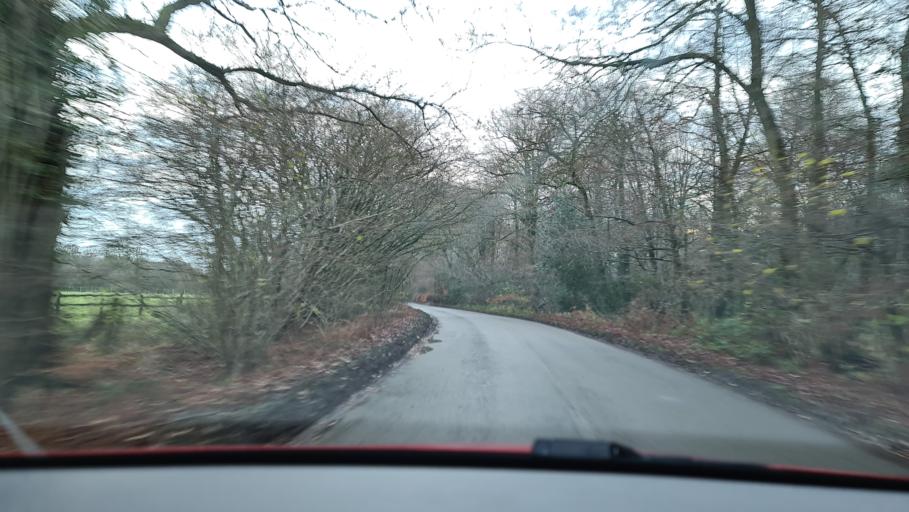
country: GB
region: England
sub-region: Buckinghamshire
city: Great Missenden
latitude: 51.7343
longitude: -0.6840
